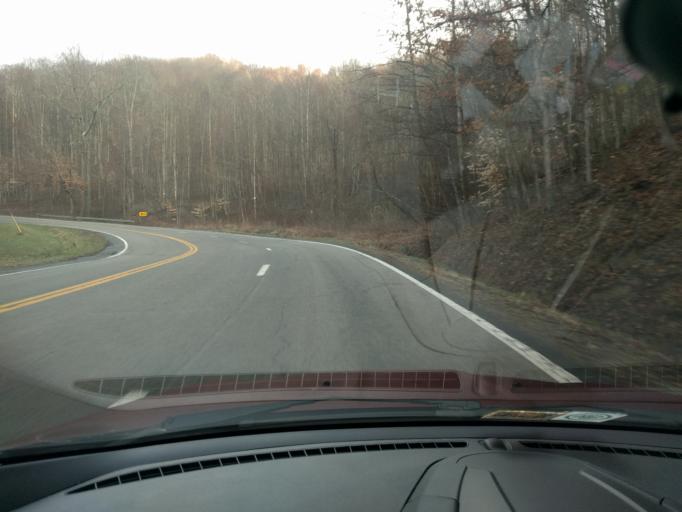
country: US
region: West Virginia
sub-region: Fayette County
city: Ansted
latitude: 38.1423
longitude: -81.1508
